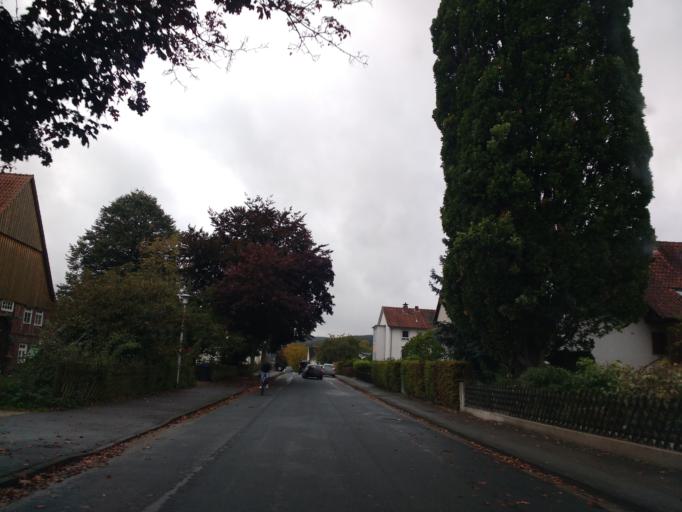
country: DE
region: Lower Saxony
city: Bad Pyrmont
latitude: 51.9885
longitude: 9.2372
